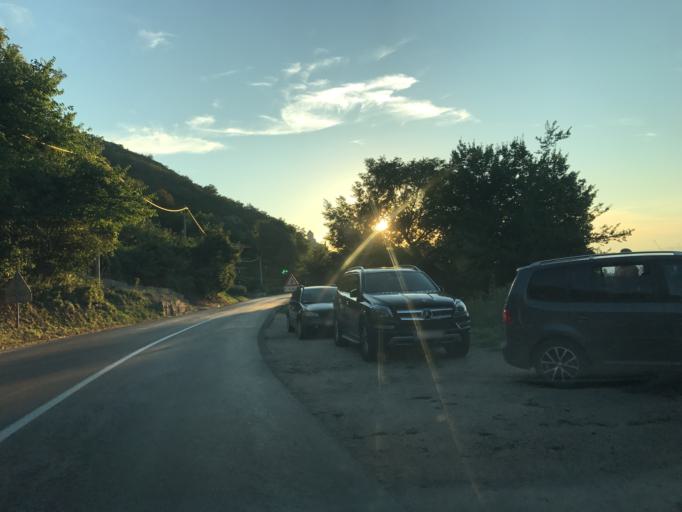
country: RO
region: Caras-Severin
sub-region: Comuna Pescari
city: Coronini
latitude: 44.6600
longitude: 21.6877
